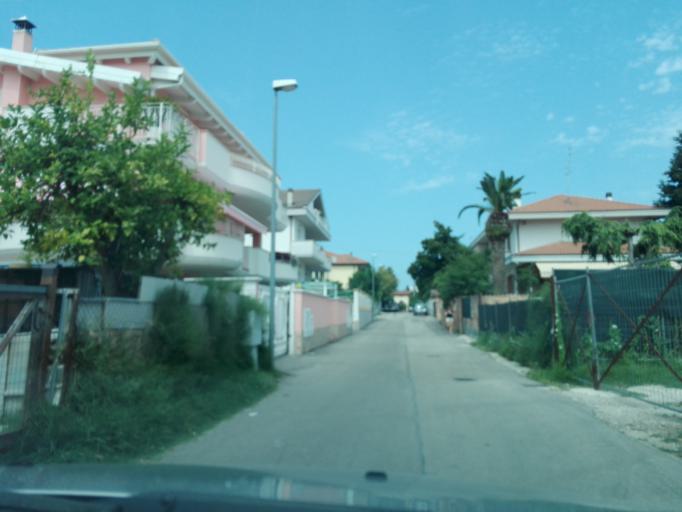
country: IT
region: Abruzzo
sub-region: Provincia di Pescara
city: Montesilvano Marina
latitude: 42.5072
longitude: 14.1385
